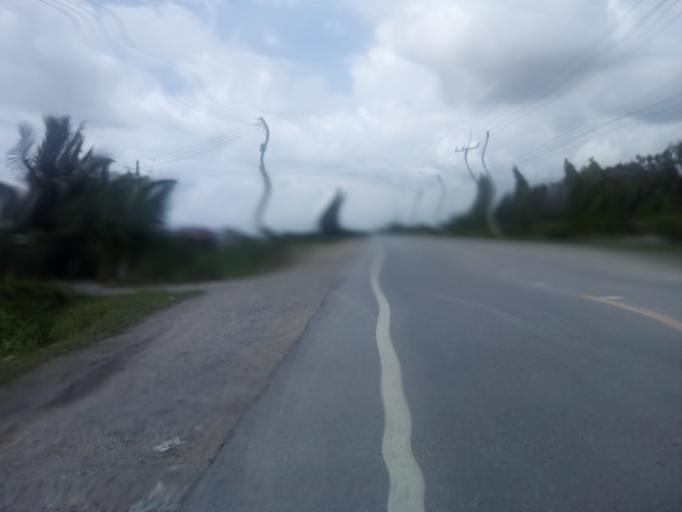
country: TH
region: Pathum Thani
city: Ban Lam Luk Ka
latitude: 14.0075
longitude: 100.8226
